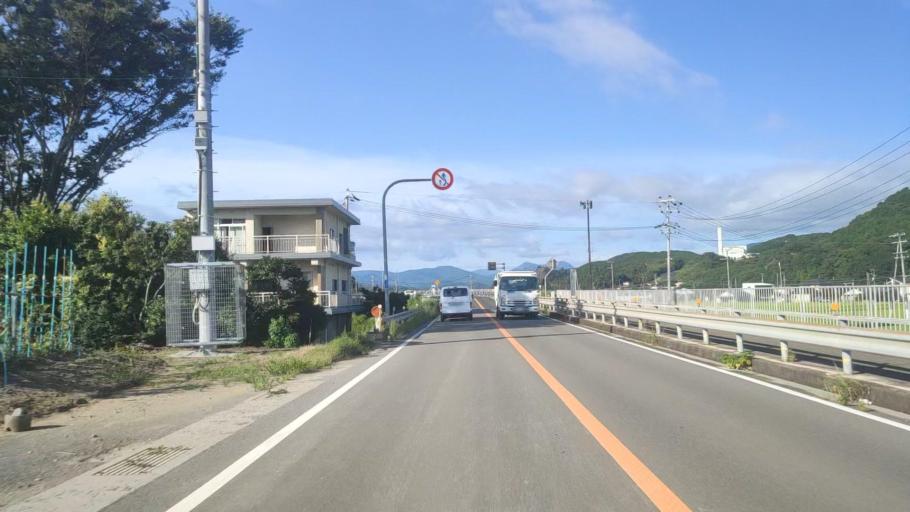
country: JP
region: Wakayama
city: Tanabe
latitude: 33.6779
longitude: 135.4089
